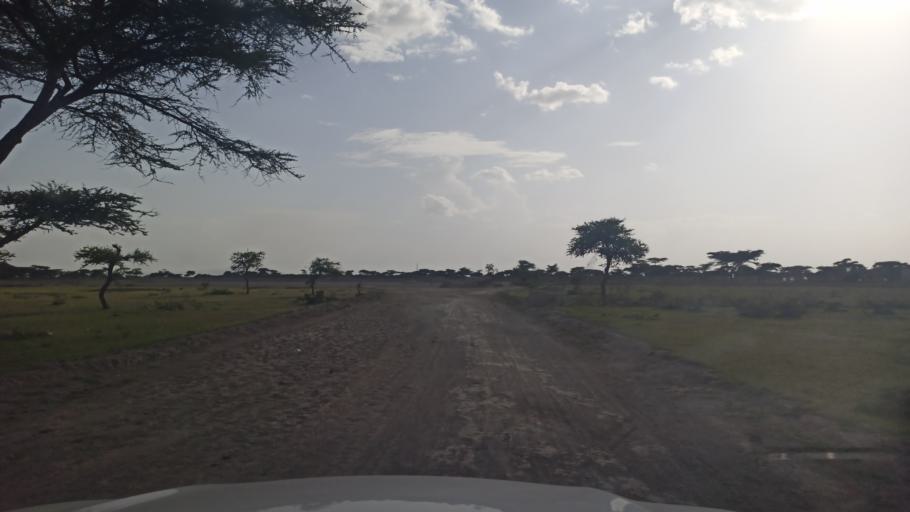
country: ET
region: Oromiya
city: Ziway
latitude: 7.6703
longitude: 38.6803
